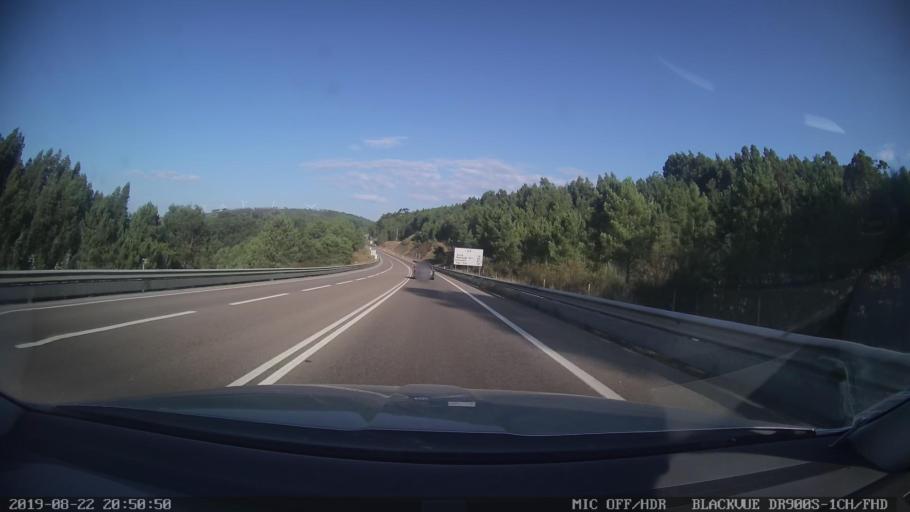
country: PT
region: Castelo Branco
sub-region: Proenca-A-Nova
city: Proenca-a-Nova
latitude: 39.7576
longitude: -7.9469
